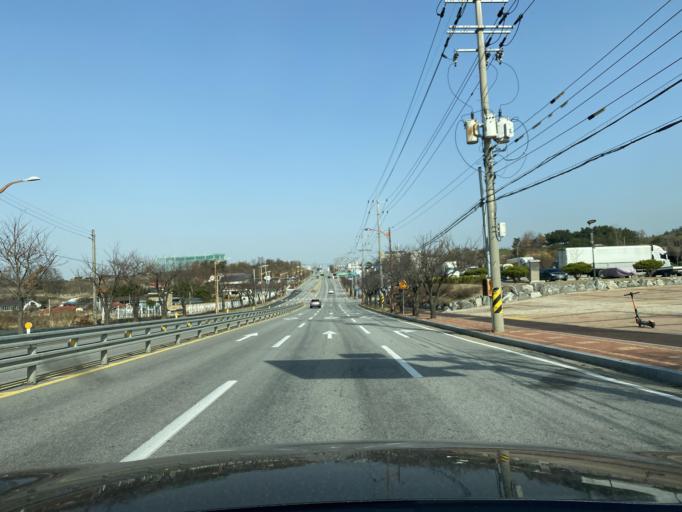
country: KR
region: Chungcheongnam-do
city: Yesan
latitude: 36.6993
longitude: 126.8379
